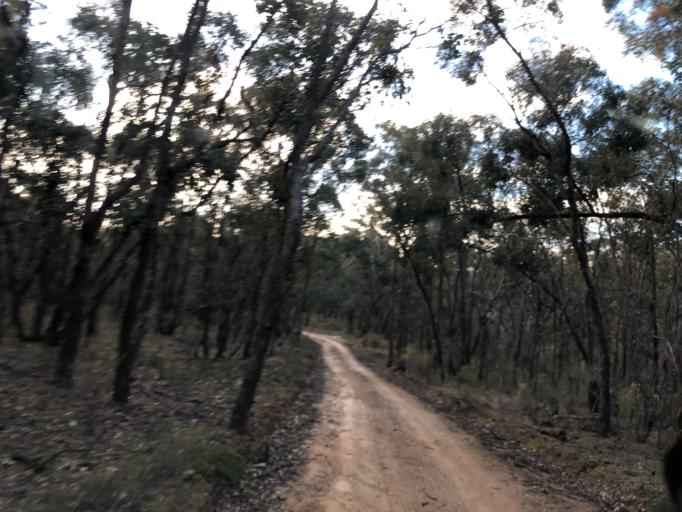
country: AU
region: Victoria
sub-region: Mount Alexander
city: Castlemaine
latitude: -37.2211
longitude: 144.2645
